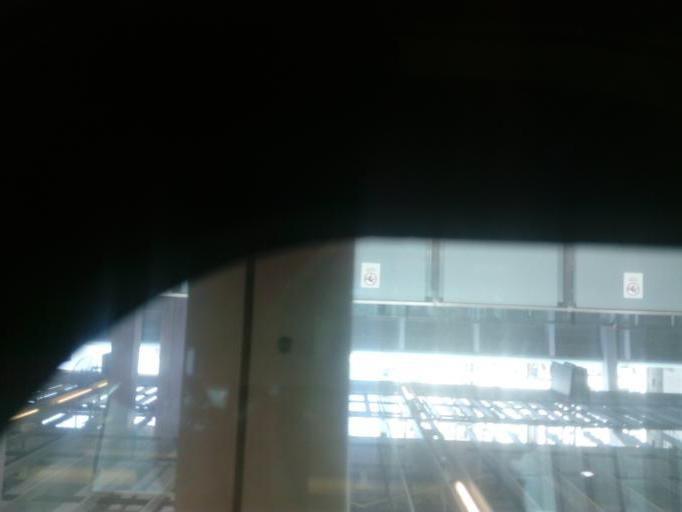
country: HK
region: Sai Kung
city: Sai Kung
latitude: 22.4244
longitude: 114.2315
